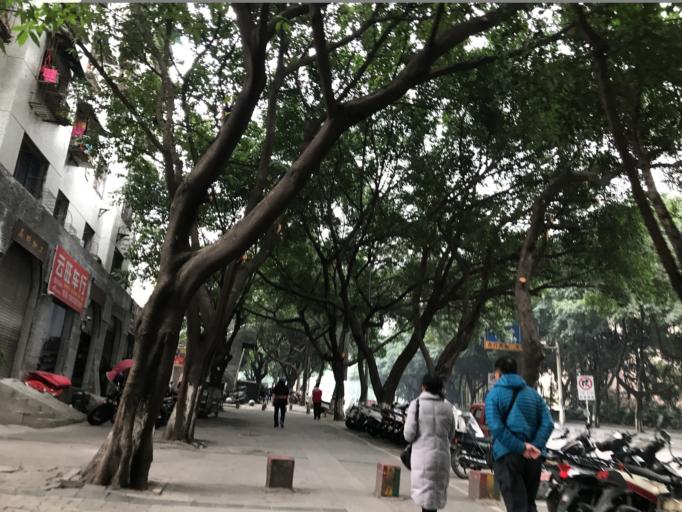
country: CN
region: Chongqing Shi
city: Chongqing
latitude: 29.5301
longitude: 106.5527
